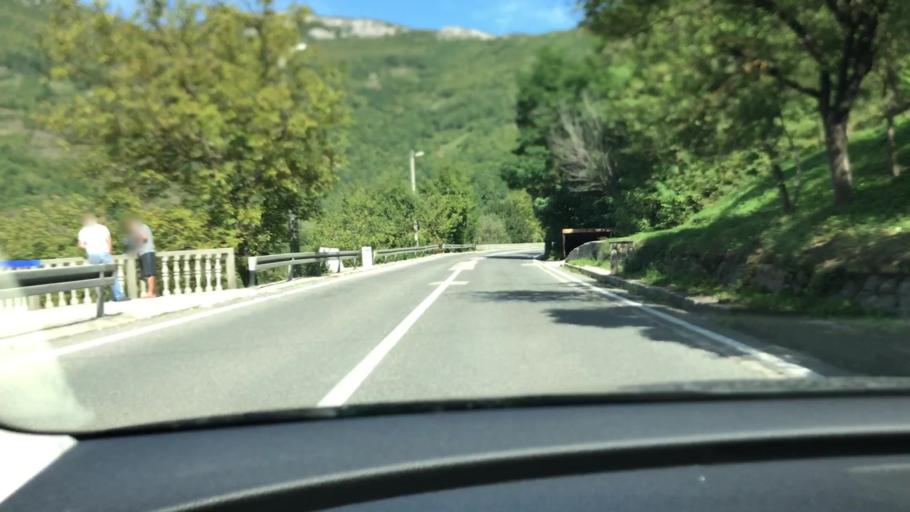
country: BA
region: Federation of Bosnia and Herzegovina
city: Jablanica
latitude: 43.6843
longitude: 17.7879
